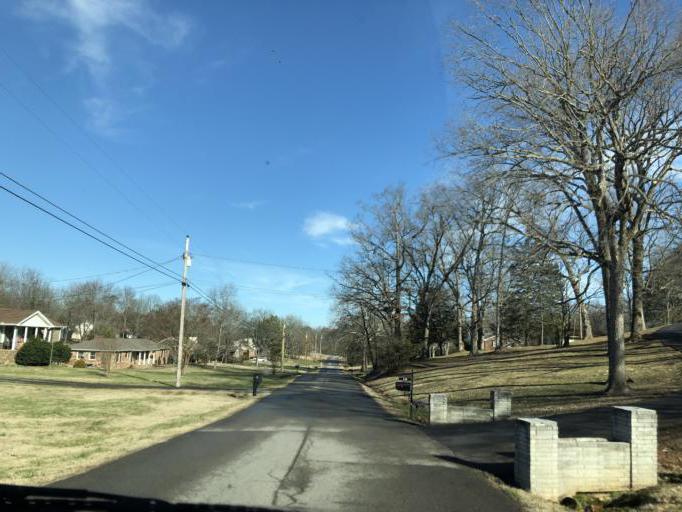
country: US
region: Tennessee
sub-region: Wilson County
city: Mount Juliet
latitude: 36.1795
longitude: -86.5255
